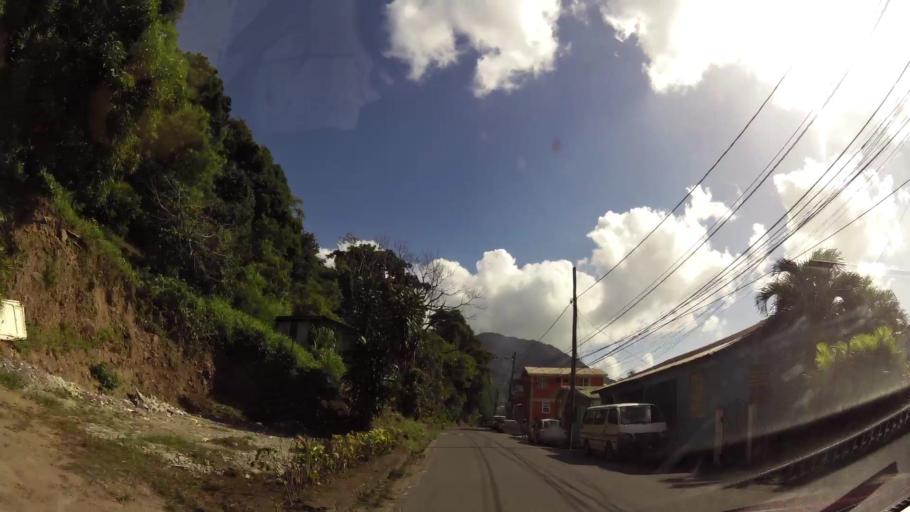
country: DM
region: Saint George
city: Roseau
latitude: 15.2884
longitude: -61.3765
